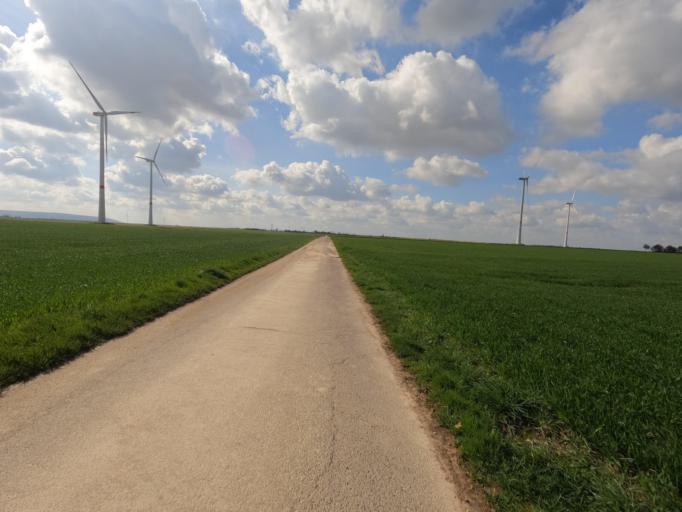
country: DE
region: North Rhine-Westphalia
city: Erkelenz
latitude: 51.0182
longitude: 6.3453
